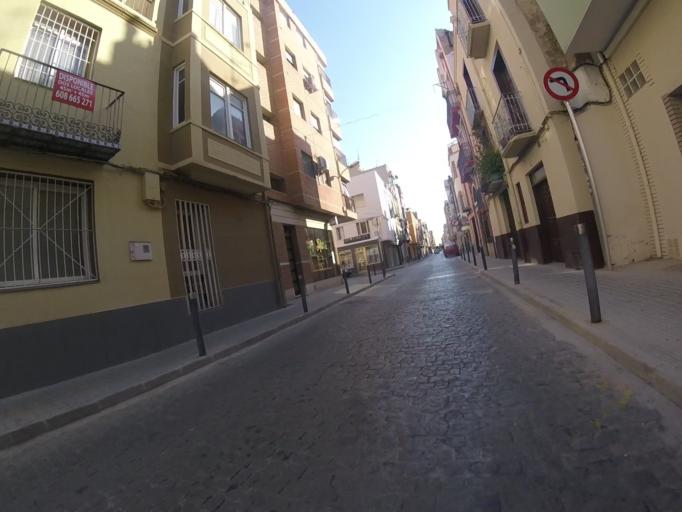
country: ES
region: Valencia
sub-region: Provincia de Castello
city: Benicarlo
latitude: 40.4200
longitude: 0.4256
